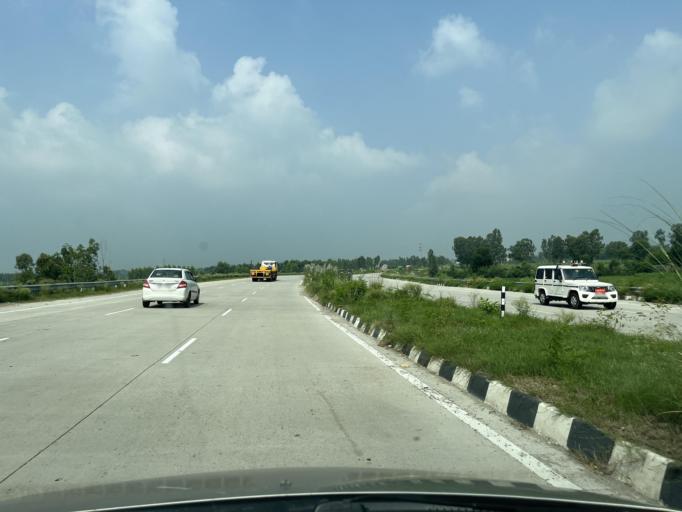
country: IN
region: Uttarakhand
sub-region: Udham Singh Nagar
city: Kashipur
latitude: 29.1633
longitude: 78.9640
